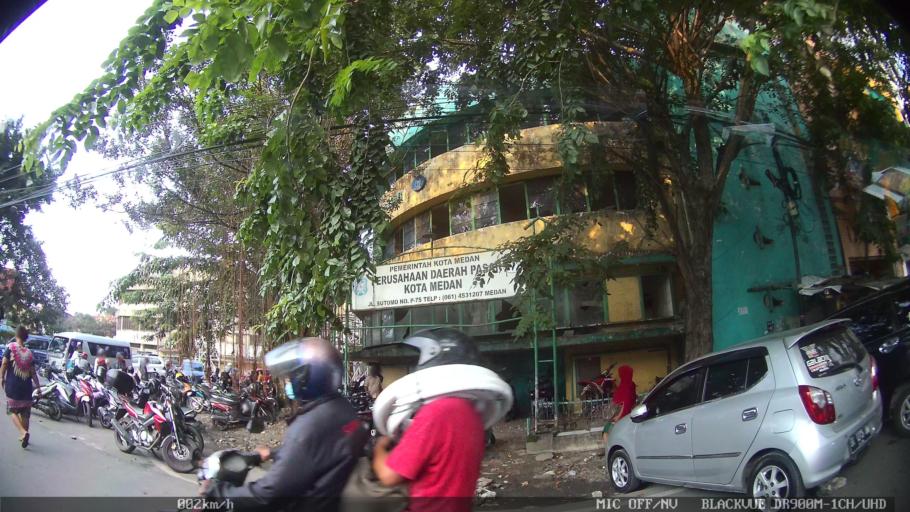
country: ID
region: North Sumatra
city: Medan
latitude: 3.5908
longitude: 98.6844
